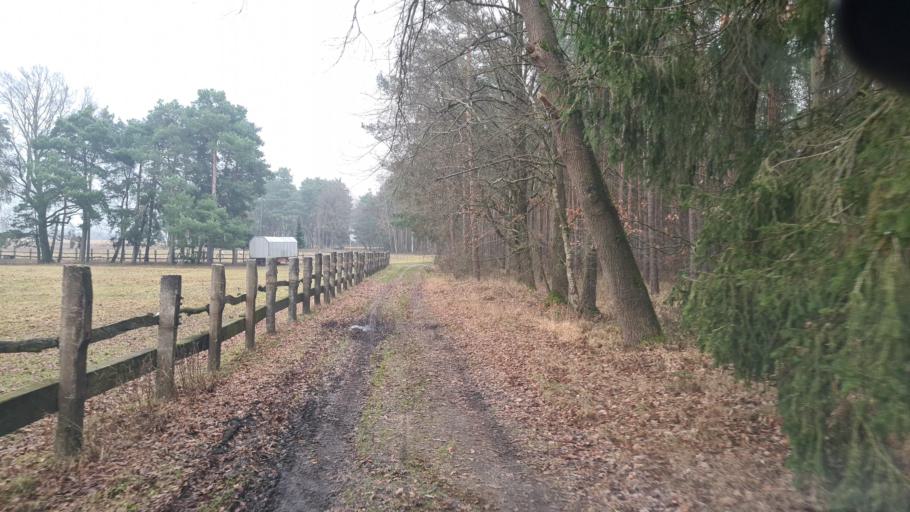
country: DE
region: Brandenburg
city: Plessa
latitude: 51.5279
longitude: 13.6304
